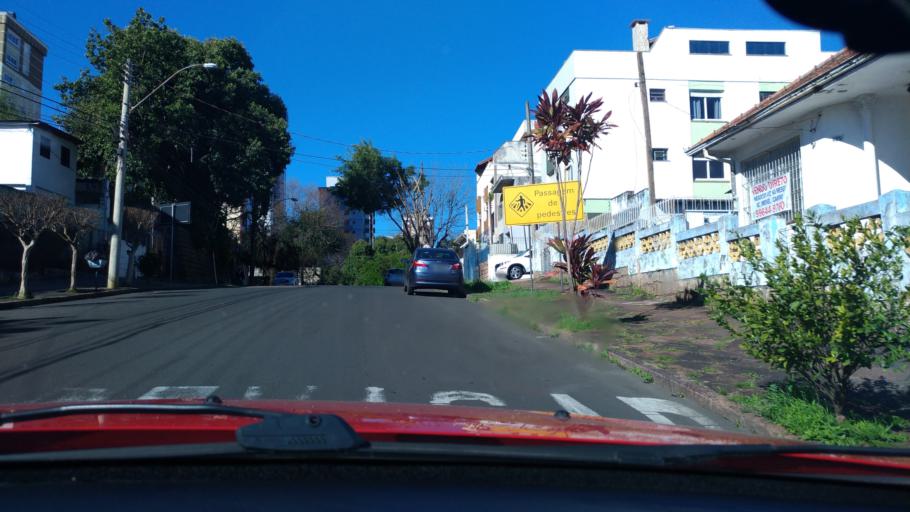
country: BR
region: Rio Grande do Sul
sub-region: Porto Alegre
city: Porto Alegre
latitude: -30.0093
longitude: -51.1652
